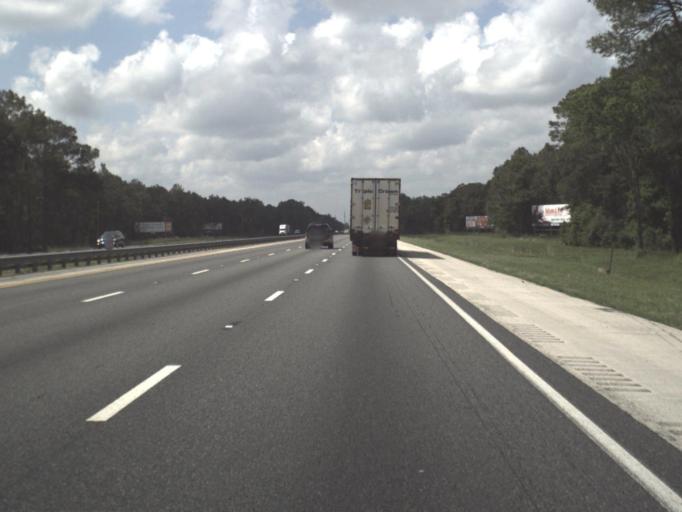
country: US
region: Florida
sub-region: Saint Johns County
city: Saint Augustine
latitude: 29.8909
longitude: -81.4038
